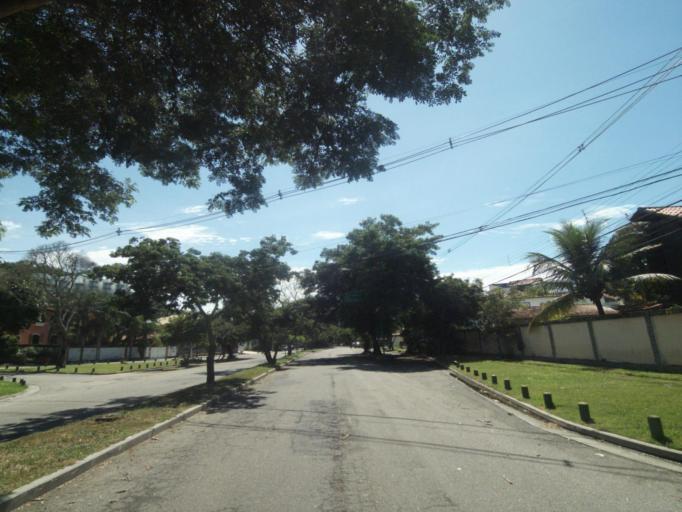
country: BR
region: Rio de Janeiro
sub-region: Niteroi
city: Niteroi
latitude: -22.9559
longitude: -43.0643
